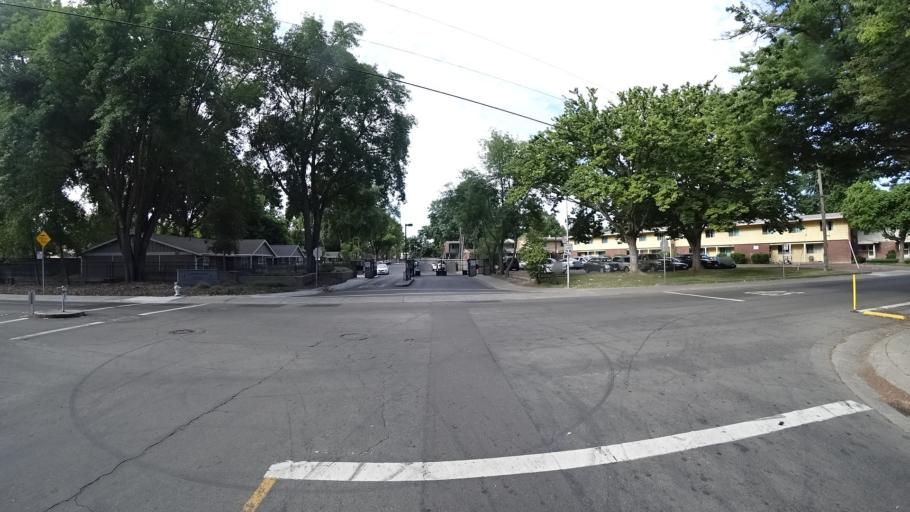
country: US
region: California
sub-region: Sacramento County
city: Sacramento
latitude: 38.5580
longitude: -121.5103
